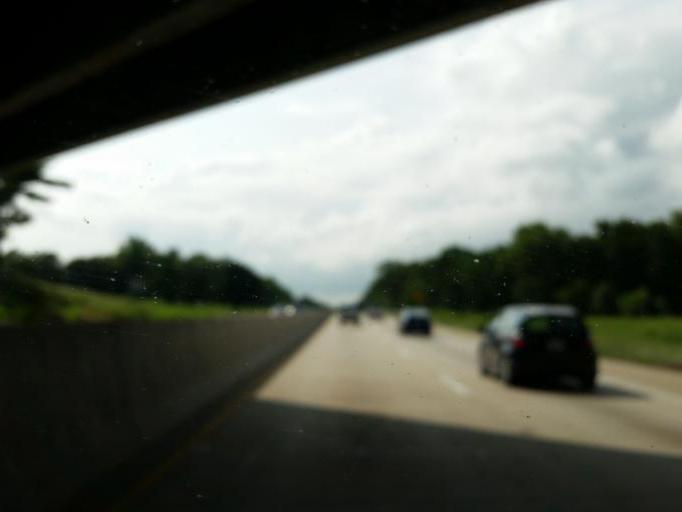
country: US
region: Pennsylvania
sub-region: Lancaster County
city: Salunga
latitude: 40.1058
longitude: -76.4288
